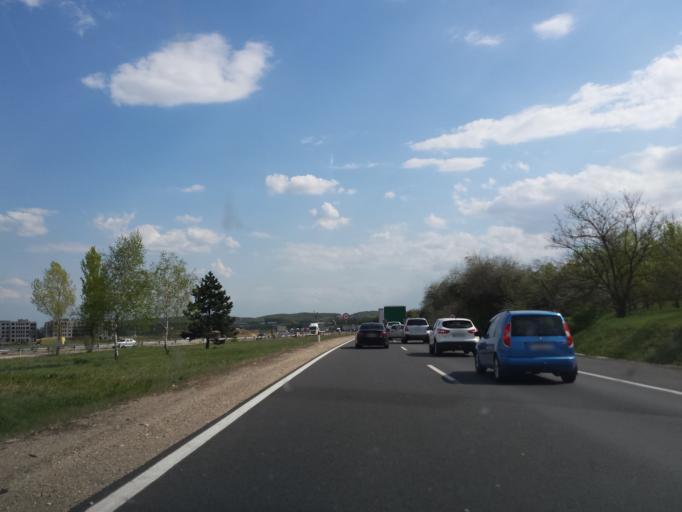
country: HU
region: Pest
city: Toeroekbalint
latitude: 47.4610
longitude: 18.8777
